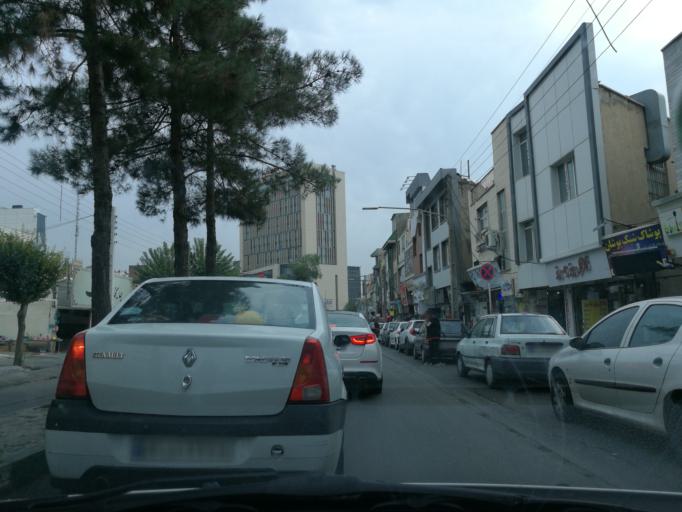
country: IR
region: Alborz
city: Karaj
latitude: 35.8454
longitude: 50.9705
